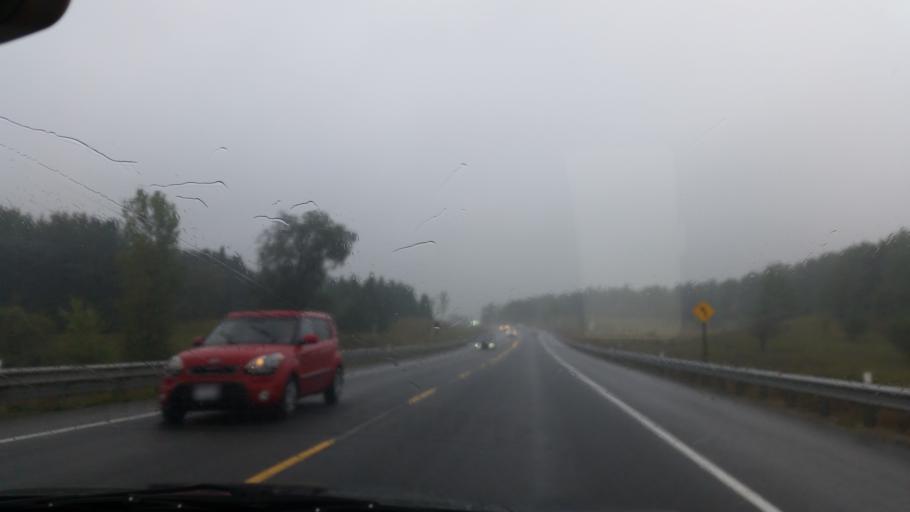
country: CA
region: Ontario
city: Stratford
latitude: 43.2607
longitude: -81.0759
